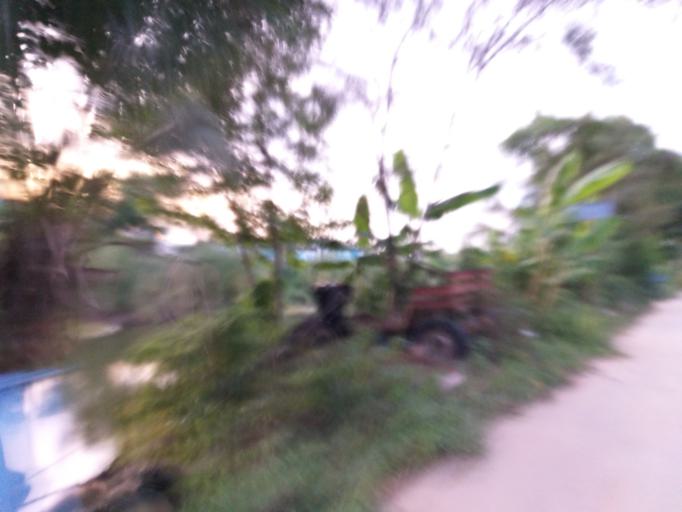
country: TH
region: Pathum Thani
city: Ban Rangsit
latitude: 14.0282
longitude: 100.8007
